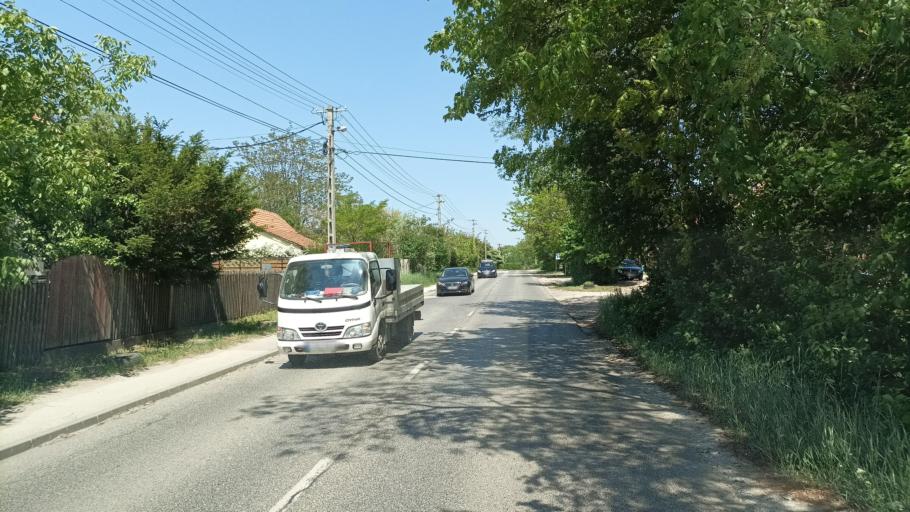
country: HU
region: Pest
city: Gyomro
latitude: 47.4213
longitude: 19.4112
